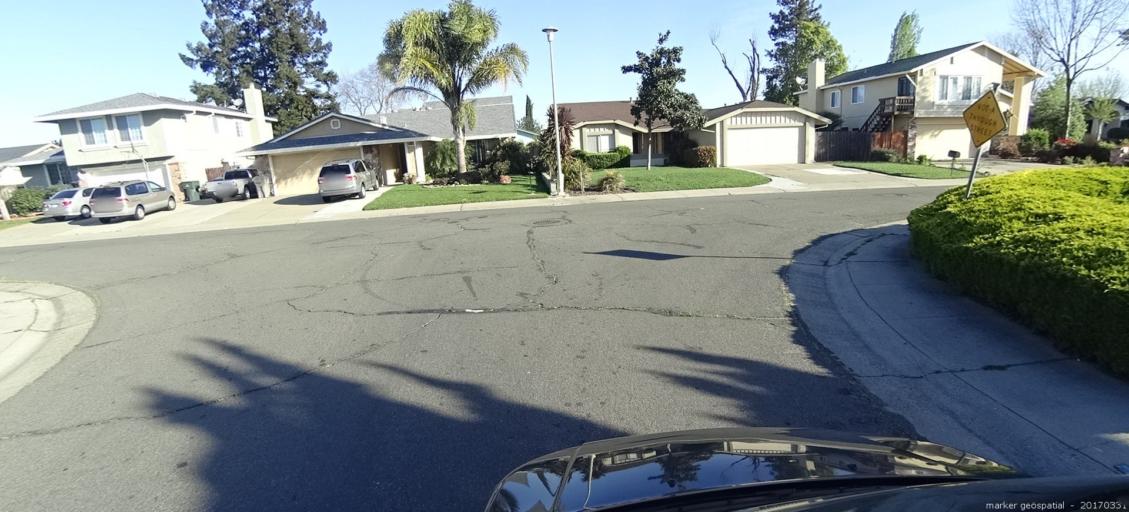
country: US
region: California
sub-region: Sacramento County
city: Parkway
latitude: 38.4697
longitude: -121.4506
